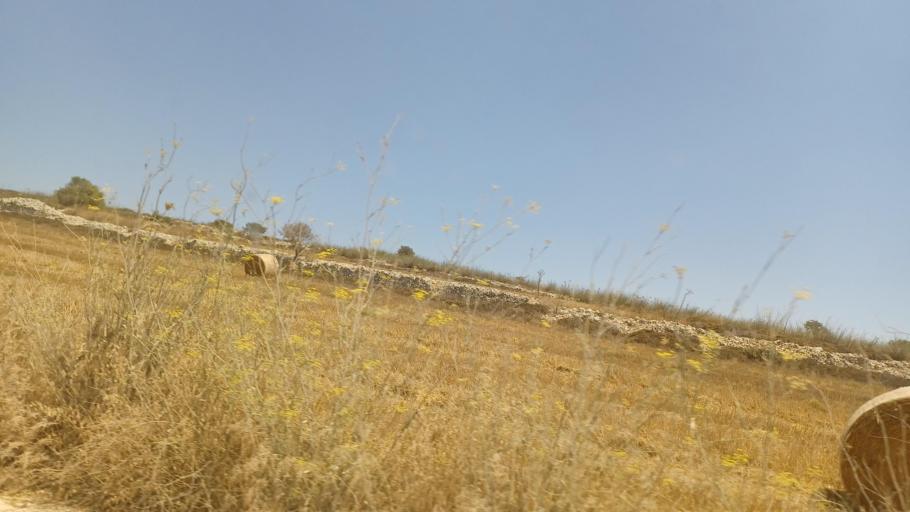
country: CY
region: Pafos
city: Pegeia
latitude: 34.9475
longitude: 32.4048
